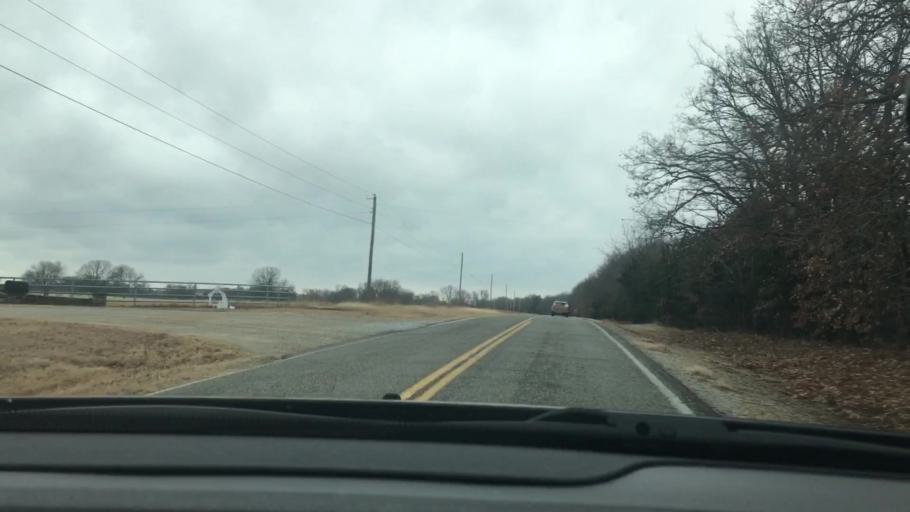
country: US
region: Oklahoma
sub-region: Johnston County
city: Tishomingo
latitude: 34.1946
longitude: -96.5780
